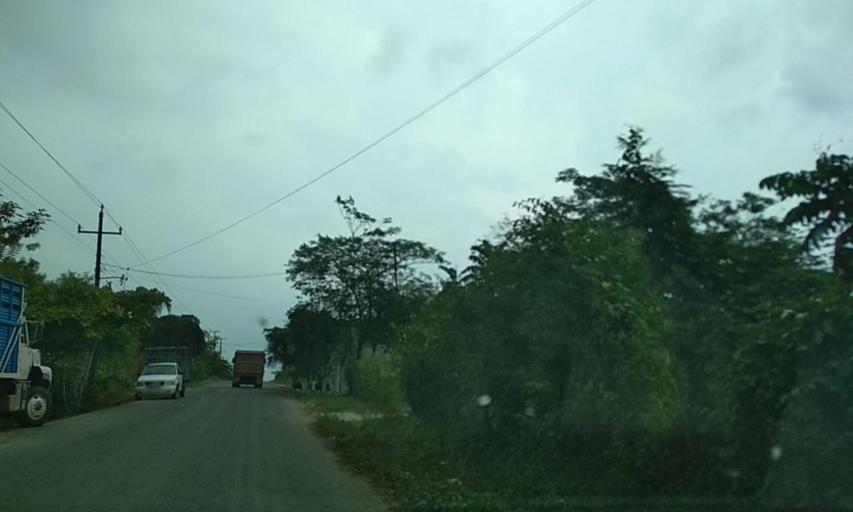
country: MX
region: Tabasco
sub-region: Huimanguillo
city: Francisco Rueda
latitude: 17.5677
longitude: -94.1120
